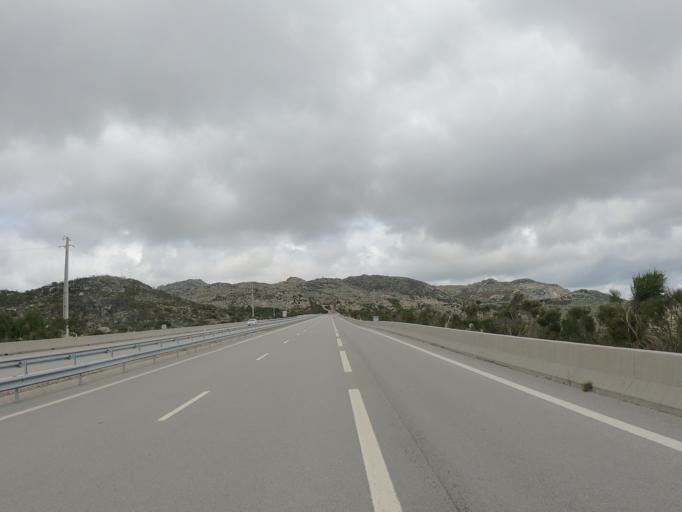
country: PT
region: Vila Real
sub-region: Vila Real
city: Vila Real
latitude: 41.3776
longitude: -7.6676
